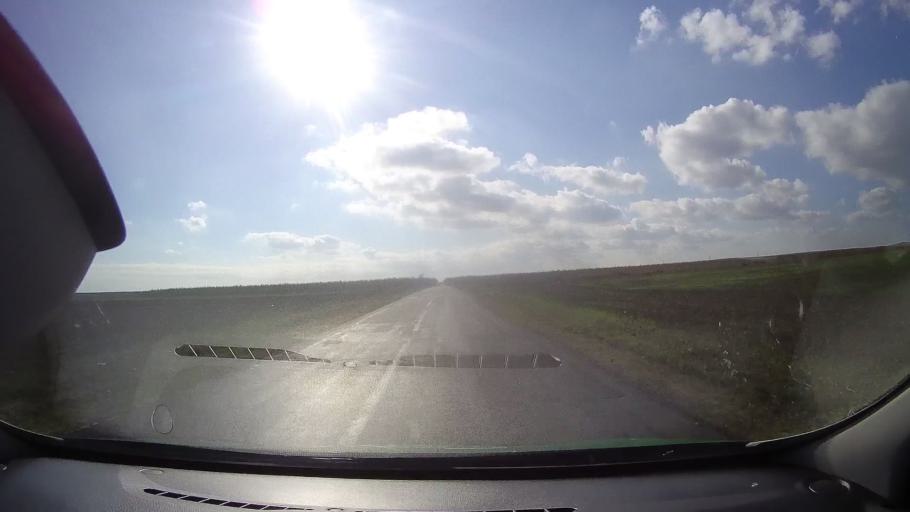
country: RO
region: Constanta
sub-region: Comuna Mihai Viteazu
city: Mihai Viteazu
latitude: 44.6184
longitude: 28.7263
